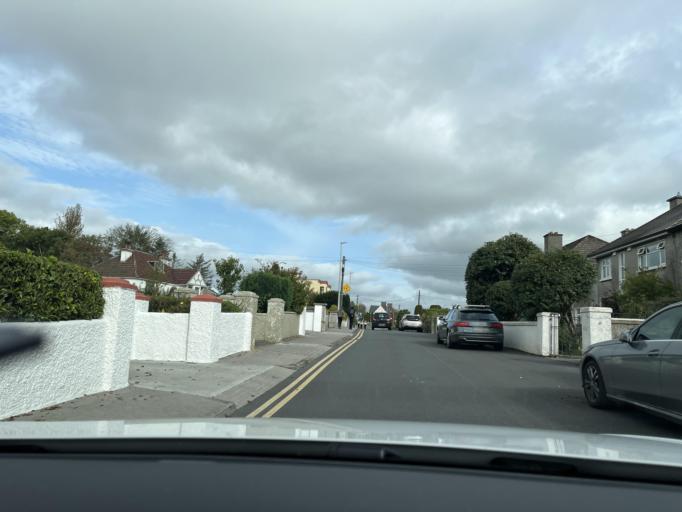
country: IE
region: Connaught
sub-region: County Leitrim
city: Carrick-on-Shannon
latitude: 53.9482
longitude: -8.0885
